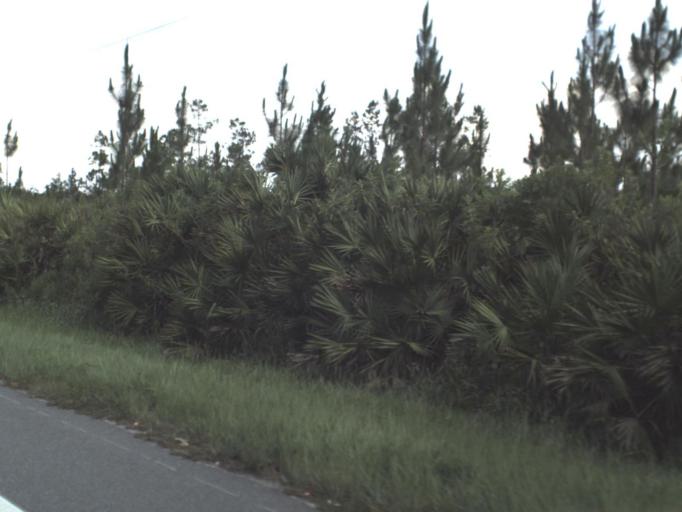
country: US
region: Florida
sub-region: Putnam County
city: Palatka
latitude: 29.6840
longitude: -81.7329
